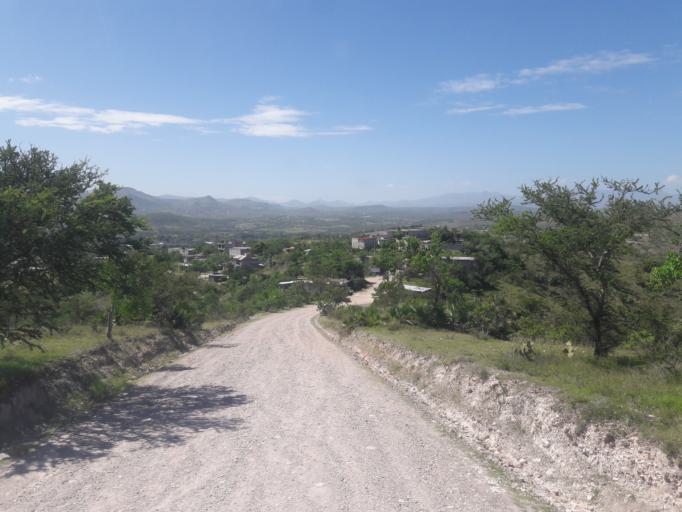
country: MX
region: Oaxaca
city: Ciudad de Huajuapam de Leon
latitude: 17.7969
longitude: -97.7992
